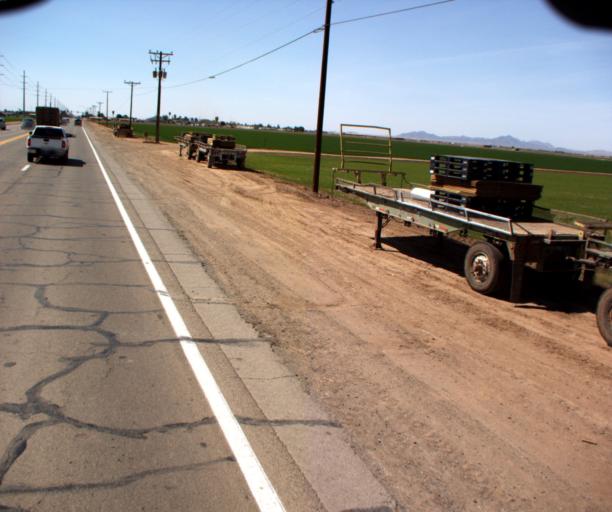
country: US
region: Arizona
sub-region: Yuma County
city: Yuma
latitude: 32.6993
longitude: -114.5164
